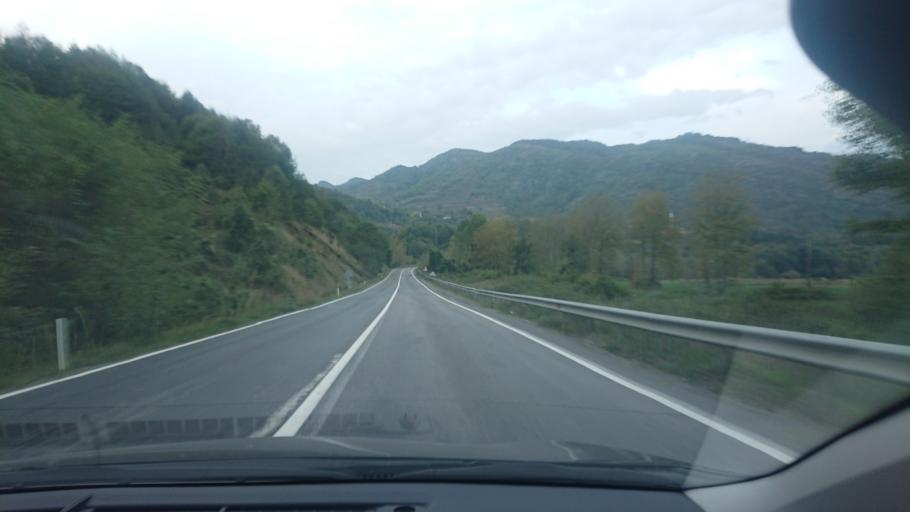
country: TR
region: Zonguldak
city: Gokcebey
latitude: 41.2792
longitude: 32.1514
